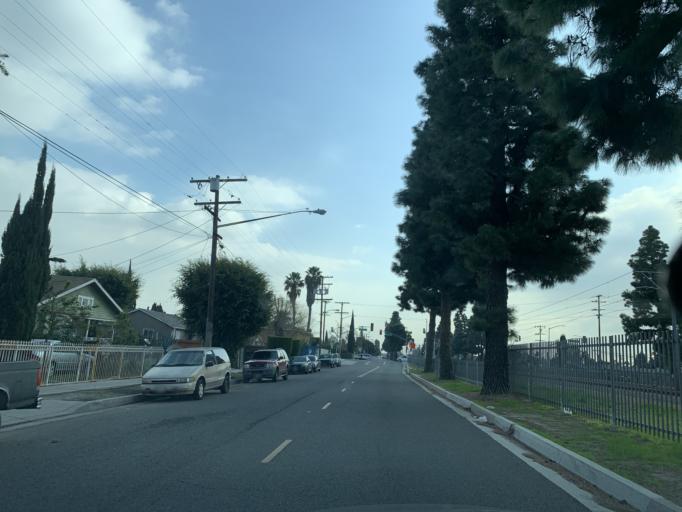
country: US
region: California
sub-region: Los Angeles County
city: Compton
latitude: 33.9120
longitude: -118.2290
